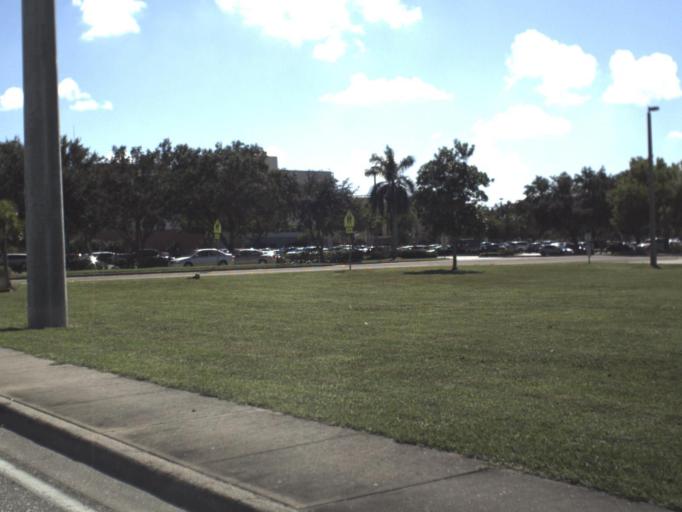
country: US
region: Florida
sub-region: Lee County
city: Lochmoor Waterway Estates
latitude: 26.6418
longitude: -81.9410
